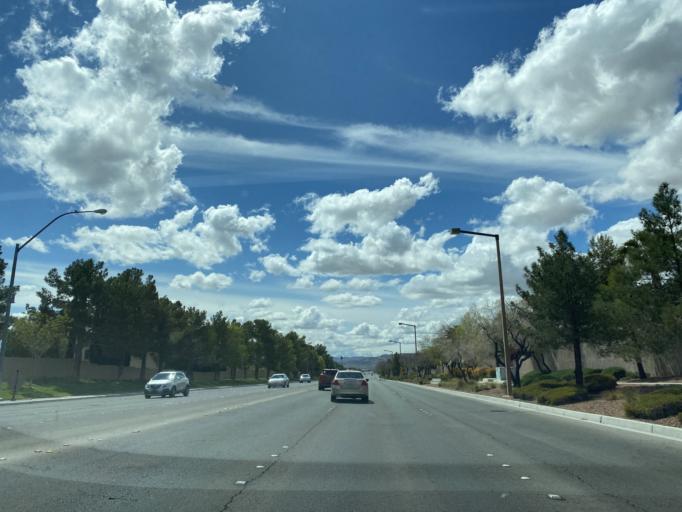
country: US
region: Nevada
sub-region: Clark County
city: Summerlin South
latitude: 36.1364
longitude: -115.3154
